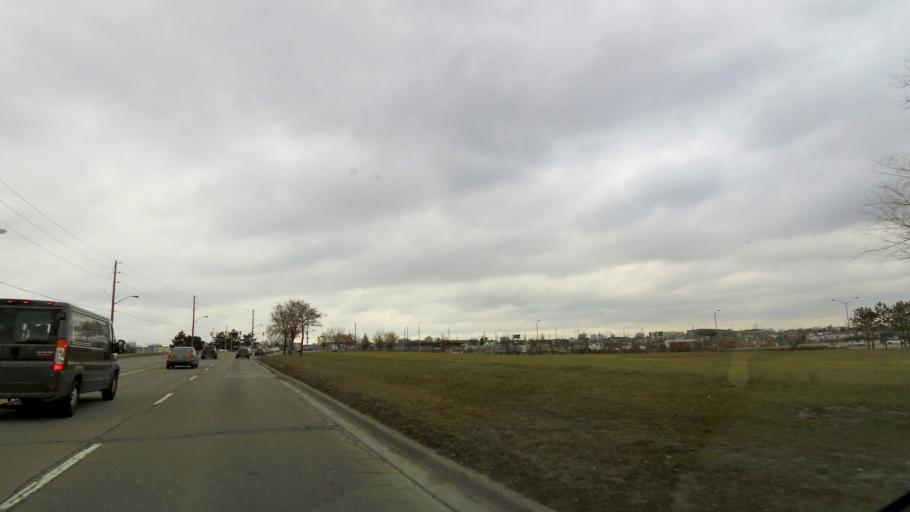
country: CA
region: Ontario
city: Concord
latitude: 43.7513
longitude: -79.4828
